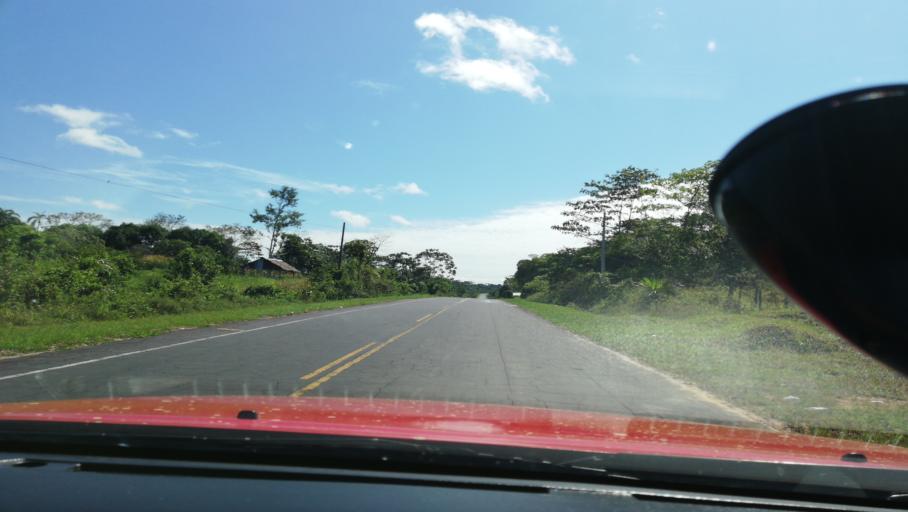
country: PE
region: Loreto
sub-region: Provincia de Loreto
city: Nauta
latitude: -4.3089
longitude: -73.5225
